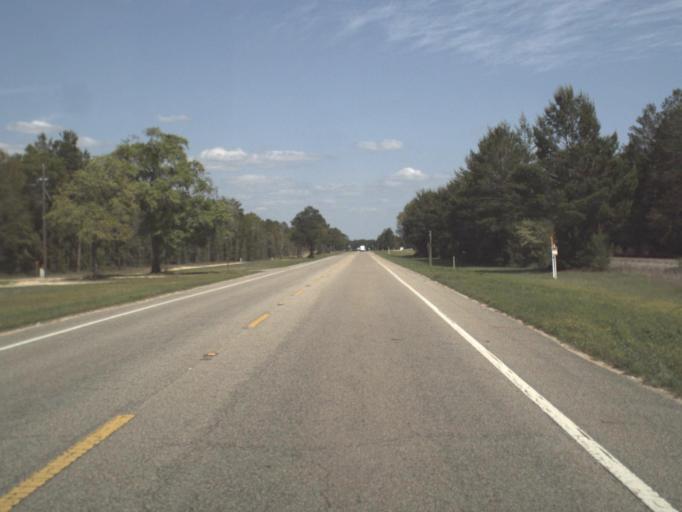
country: US
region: Florida
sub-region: Okaloosa County
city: Crestview
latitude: 30.7433
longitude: -86.4011
